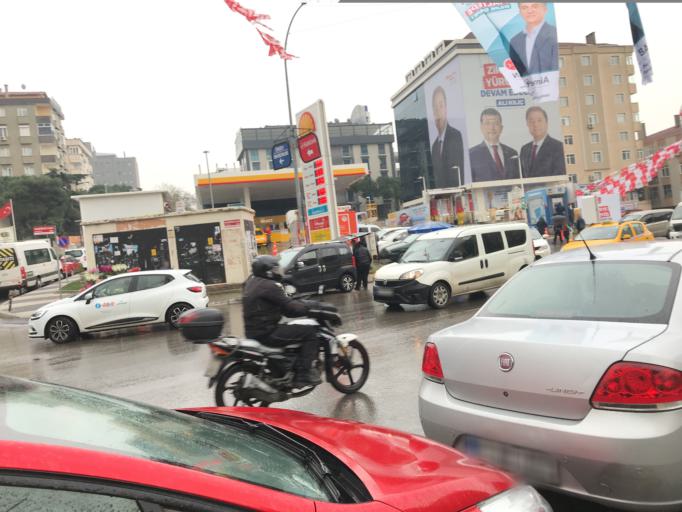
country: TR
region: Istanbul
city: Maltepe
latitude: 40.9379
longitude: 29.1408
